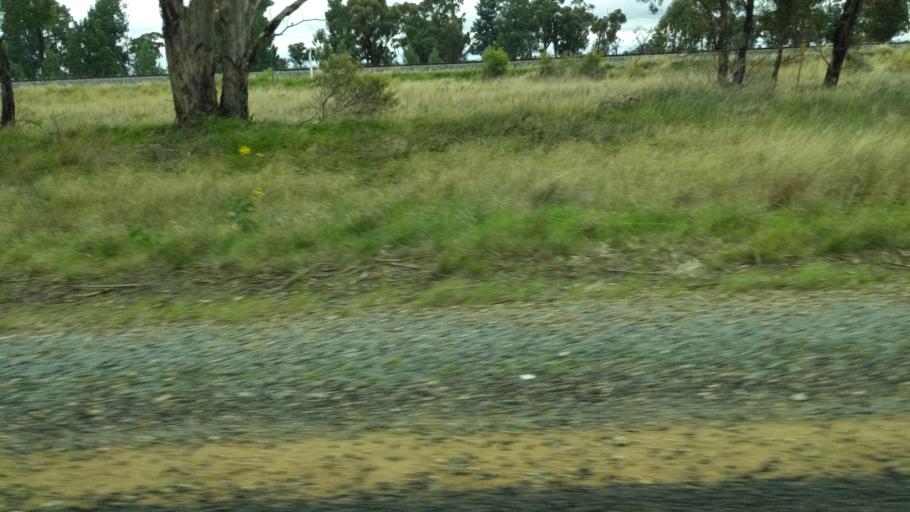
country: AU
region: New South Wales
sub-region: Coolamon
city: Coolamon
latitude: -34.7615
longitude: 146.8892
